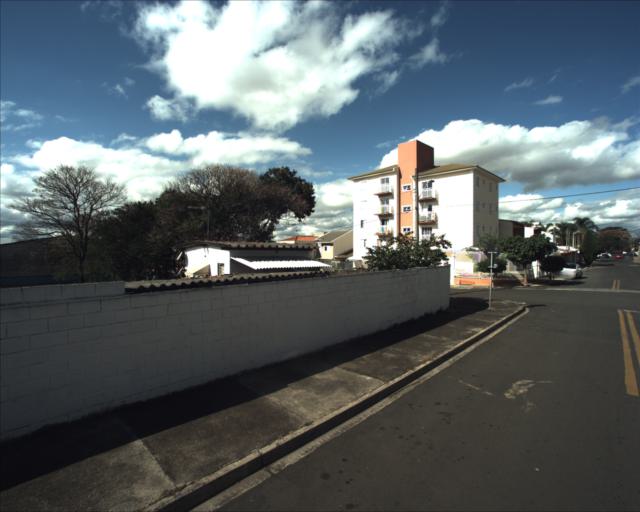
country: BR
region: Sao Paulo
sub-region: Sorocaba
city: Sorocaba
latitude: -23.4855
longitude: -47.4768
